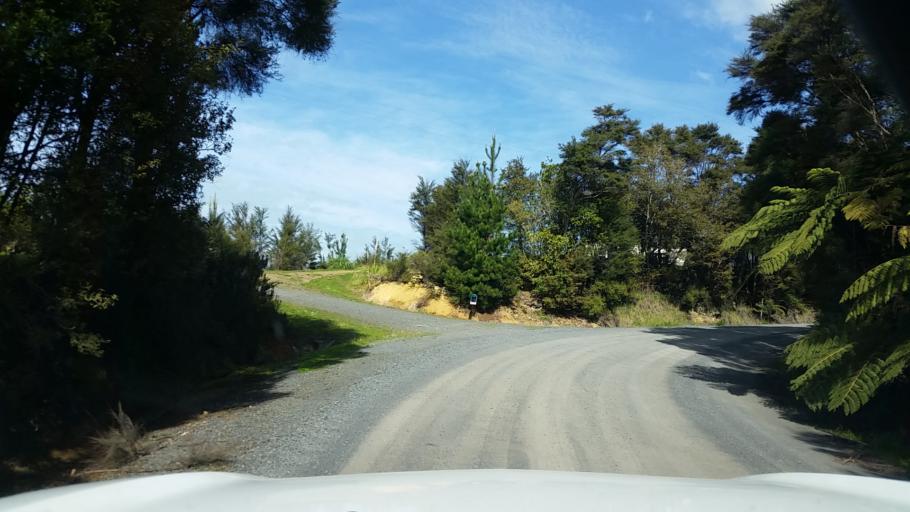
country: NZ
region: Waikato
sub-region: Hauraki District
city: Ngatea
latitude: -37.4494
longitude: 175.4748
